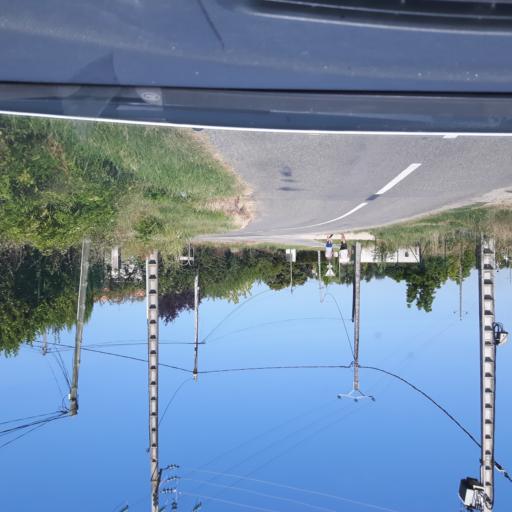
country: FR
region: Midi-Pyrenees
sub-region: Departement de la Haute-Garonne
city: Bouloc
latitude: 43.7715
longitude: 1.3984
